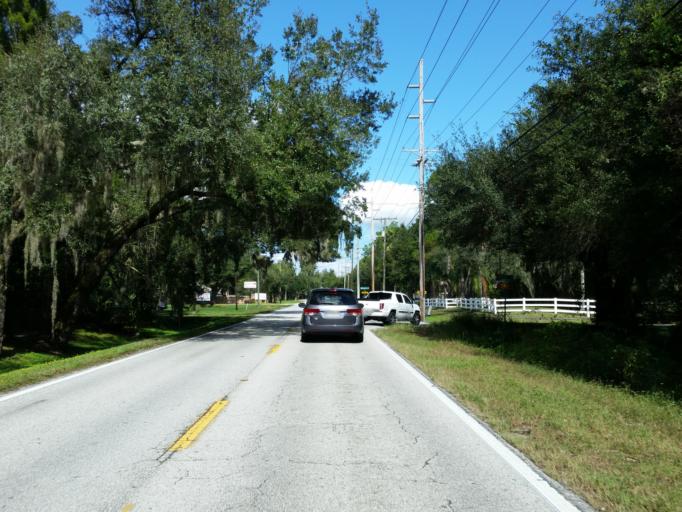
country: US
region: Florida
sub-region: Hillsborough County
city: Bloomingdale
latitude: 27.8640
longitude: -82.2692
